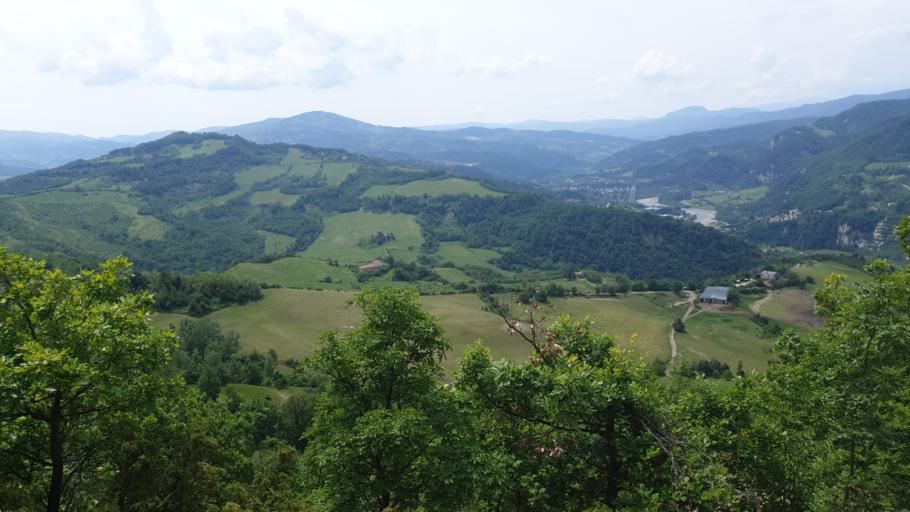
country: IT
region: Emilia-Romagna
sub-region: Provincia di Bologna
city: Vado
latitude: 44.3458
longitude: 11.2886
